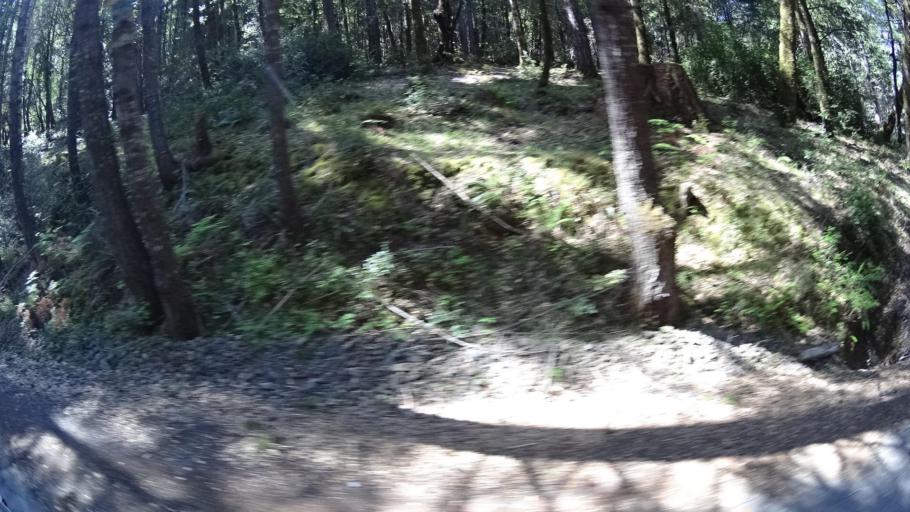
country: US
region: California
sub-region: Humboldt County
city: Redway
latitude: 40.1346
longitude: -123.9866
